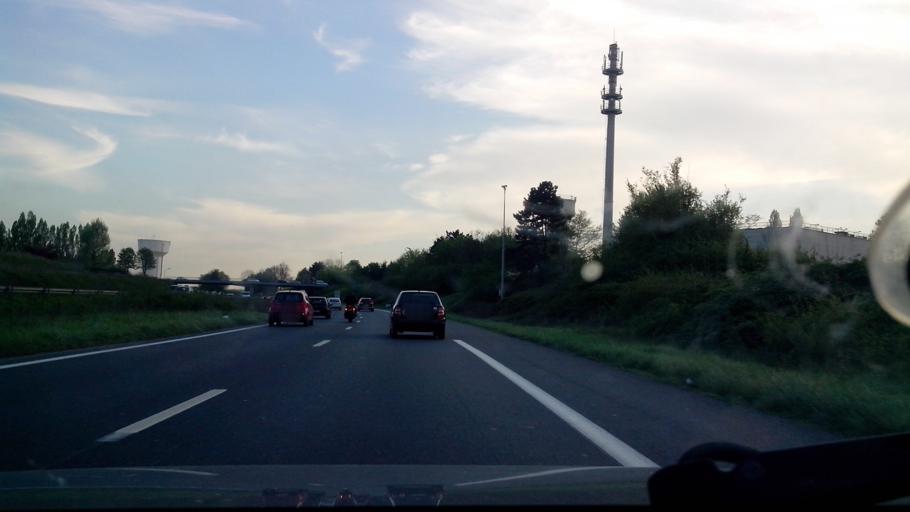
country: FR
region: Ile-de-France
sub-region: Departement de l'Essonne
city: Saclay
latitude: 48.7318
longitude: 2.1668
